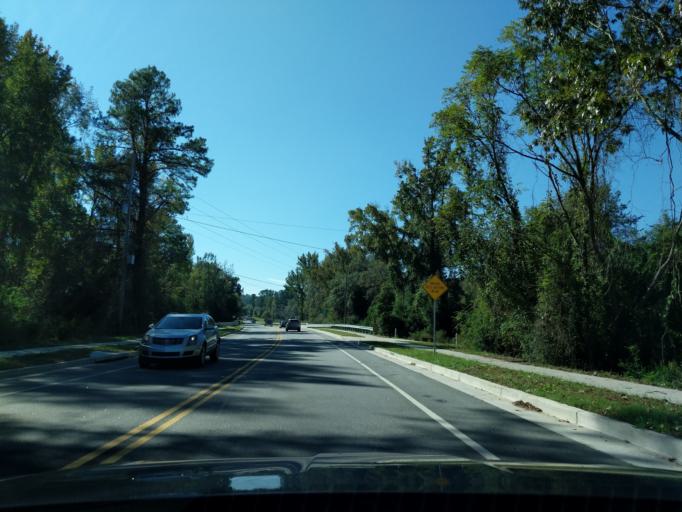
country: US
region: Georgia
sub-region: Richmond County
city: Hephzibah
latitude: 33.3460
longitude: -82.0045
